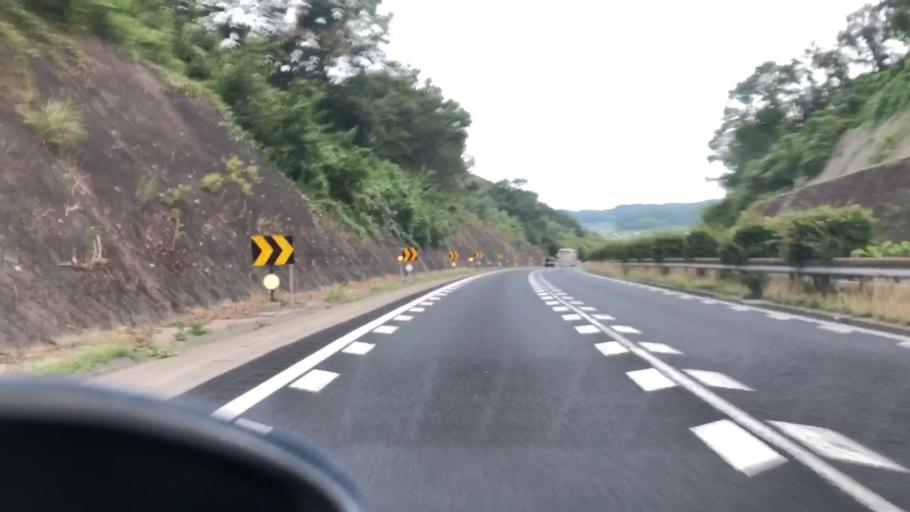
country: JP
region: Hyogo
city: Yashiro
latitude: 34.9106
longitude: 135.0550
